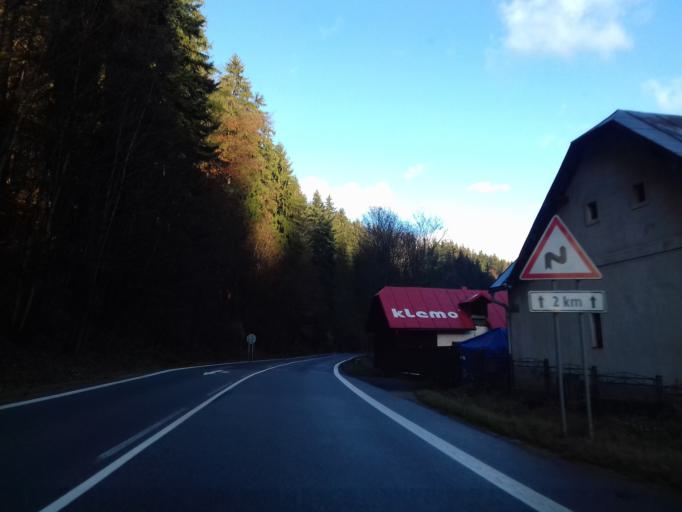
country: SK
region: Banskobystricky
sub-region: Okres Banska Bystrica
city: Banska Bystrica
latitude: 48.7953
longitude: 19.0989
